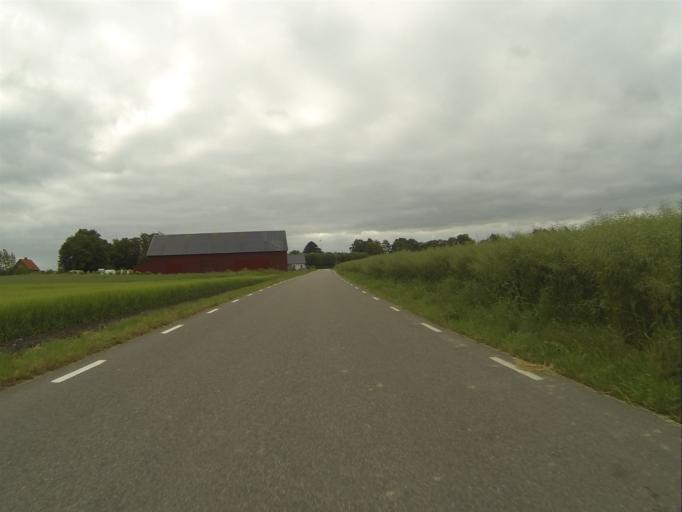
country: SE
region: Skane
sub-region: Staffanstorps Kommun
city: Staffanstorp
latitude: 55.6614
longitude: 13.2571
